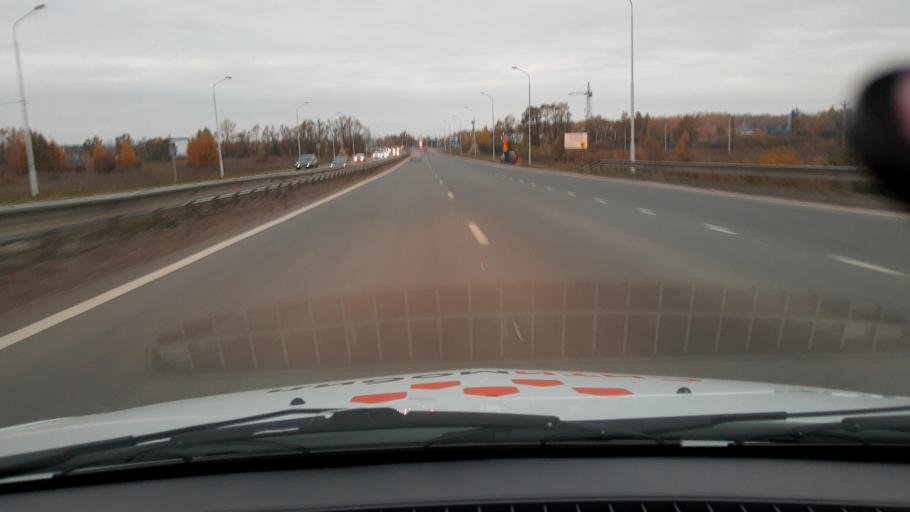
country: RU
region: Bashkortostan
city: Kabakovo
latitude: 54.6542
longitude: 56.0823
